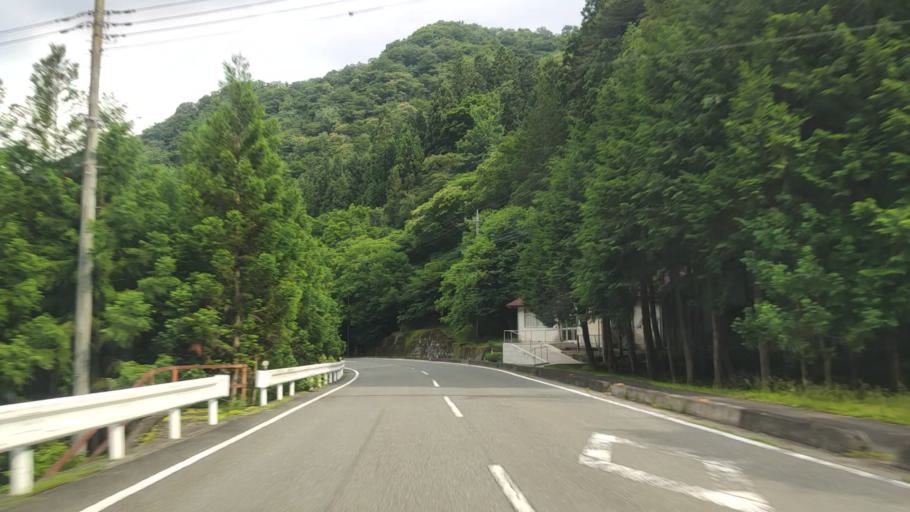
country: JP
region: Gunma
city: Tomioka
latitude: 36.0541
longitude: 138.8612
